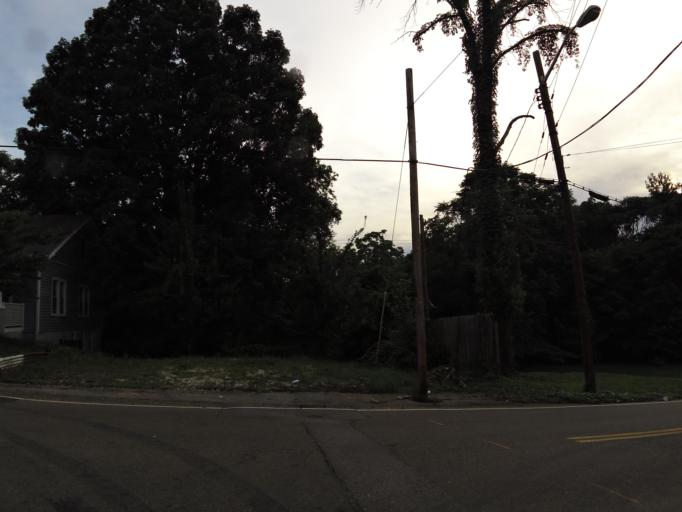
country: US
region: Tennessee
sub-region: Knox County
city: Knoxville
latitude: 35.9940
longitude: -83.9151
